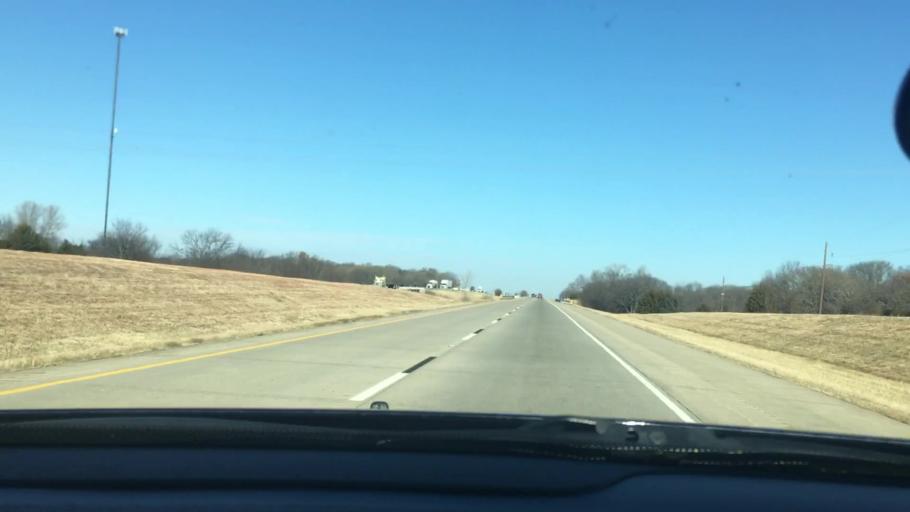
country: US
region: Oklahoma
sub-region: Love County
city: Marietta
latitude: 34.0106
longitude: -97.1427
